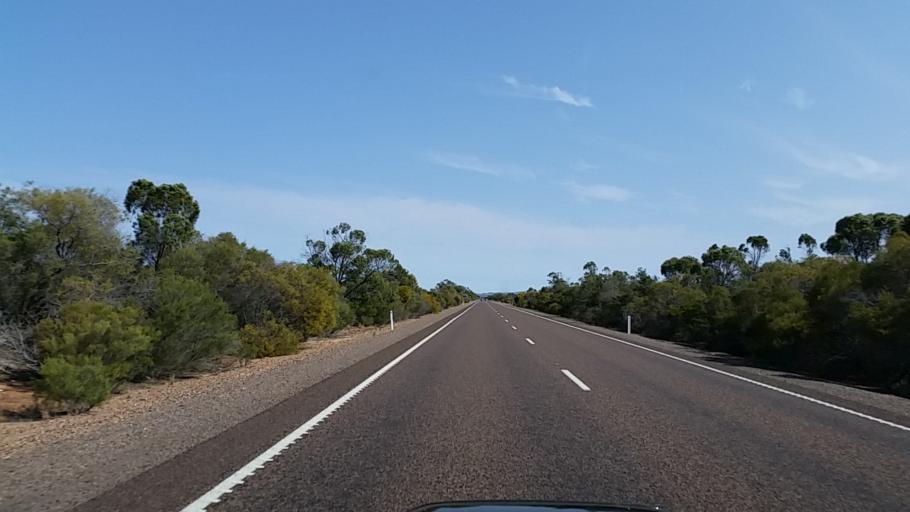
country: AU
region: South Australia
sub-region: Port Augusta
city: Port Augusta West
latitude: -32.6674
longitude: 137.5279
